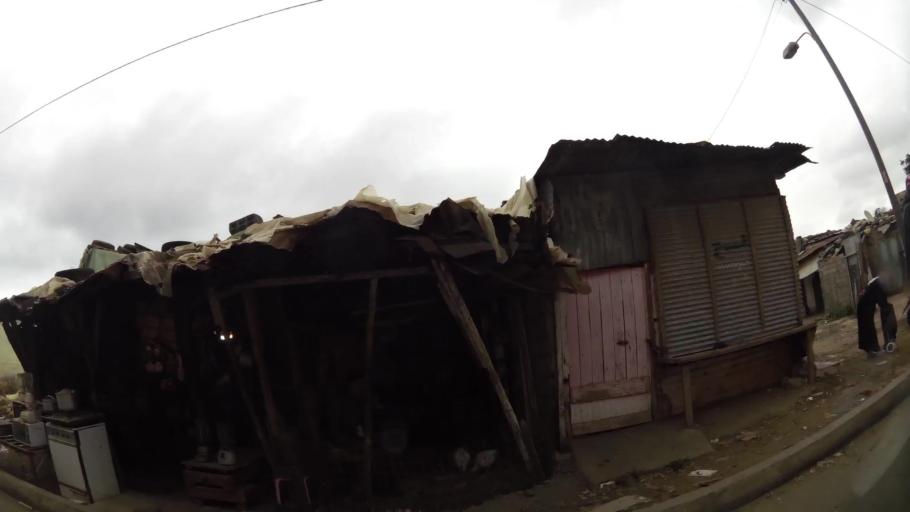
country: MA
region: Rabat-Sale-Zemmour-Zaer
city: Sale
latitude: 34.0426
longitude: -6.8042
